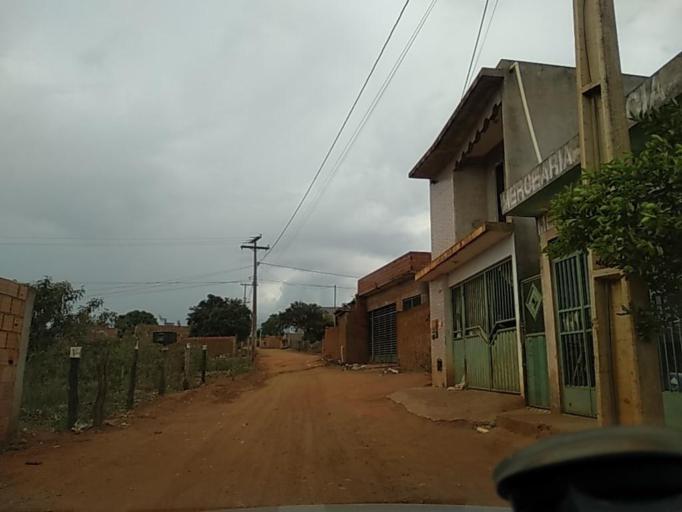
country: BR
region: Bahia
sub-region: Caetite
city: Caetite
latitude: -14.0506
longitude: -42.4749
